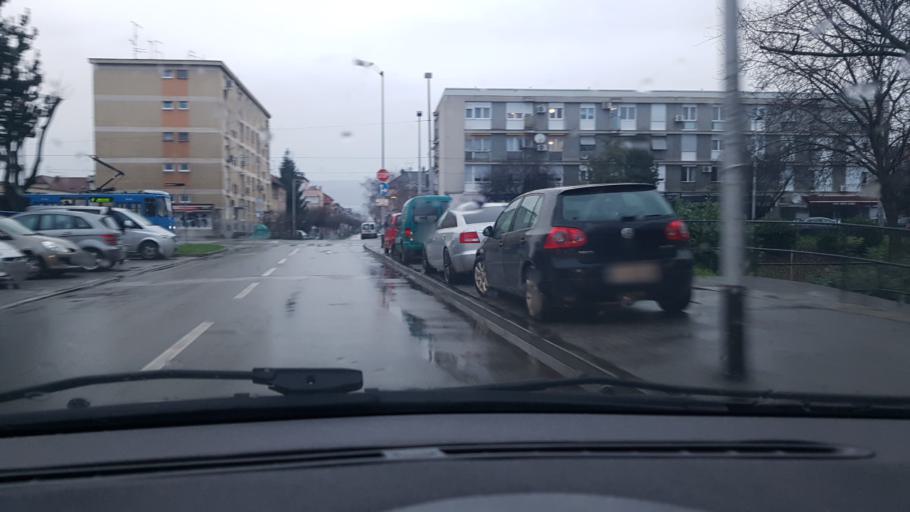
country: HR
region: Grad Zagreb
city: Jankomir
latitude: 45.7969
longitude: 15.9399
